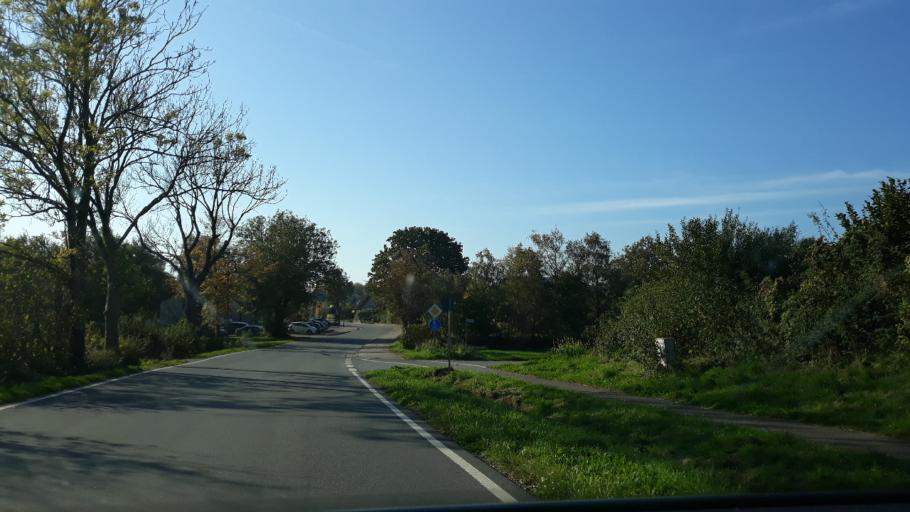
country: DE
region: Schleswig-Holstein
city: Boklund
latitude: 54.6076
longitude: 9.5846
